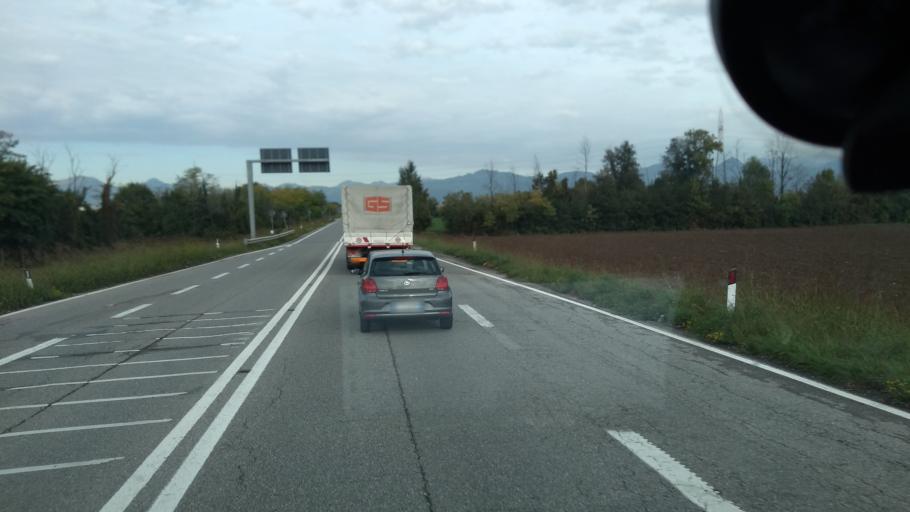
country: IT
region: Lombardy
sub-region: Provincia di Bergamo
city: Grassobbio
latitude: 45.6387
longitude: 9.7119
